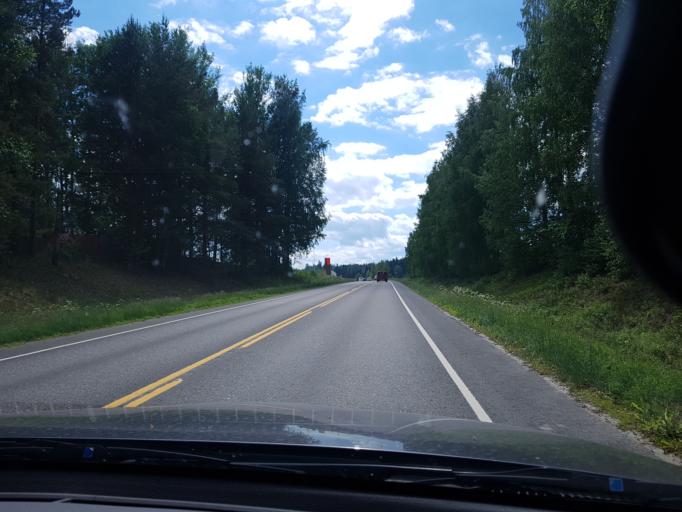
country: FI
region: Pirkanmaa
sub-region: Tampere
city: Paelkaene
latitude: 61.2603
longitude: 24.3534
